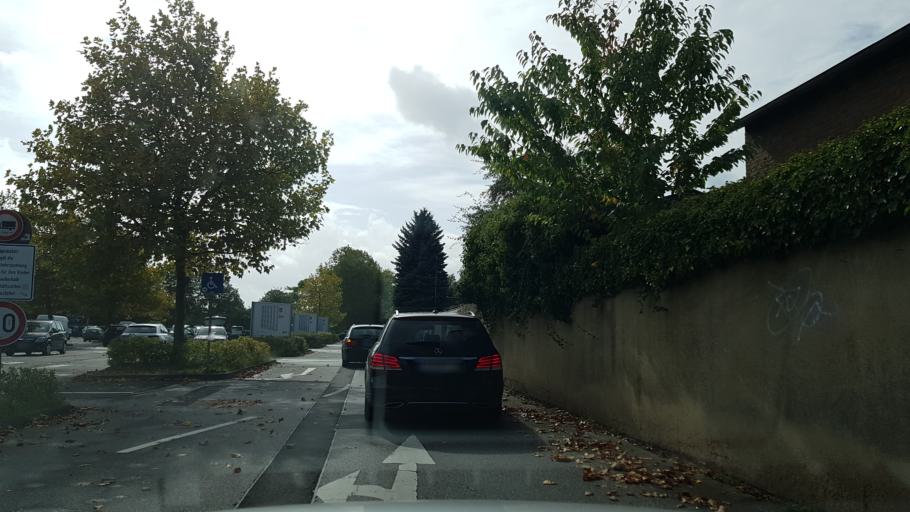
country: DE
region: North Rhine-Westphalia
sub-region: Regierungsbezirk Dusseldorf
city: Kaarst
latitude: 51.2187
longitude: 6.6268
